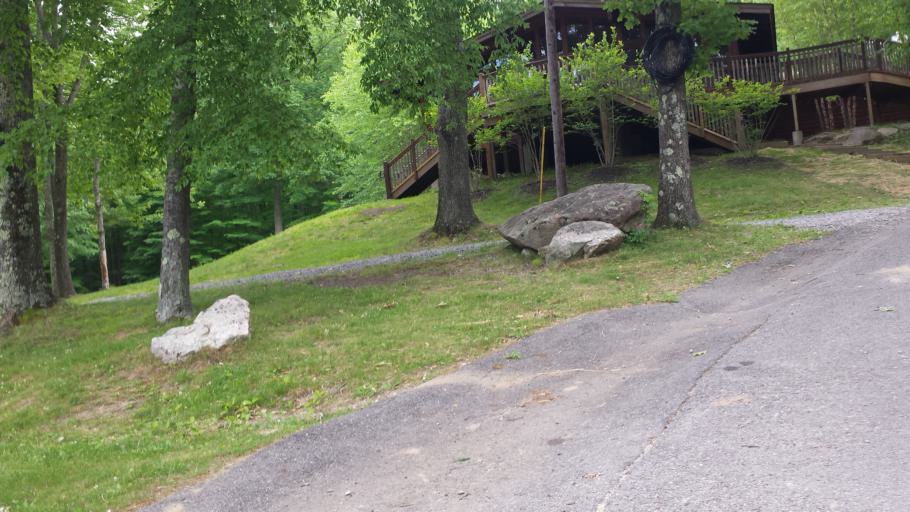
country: US
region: New York
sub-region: Putnam County
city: Peach Lake
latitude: 41.3091
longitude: -73.5692
